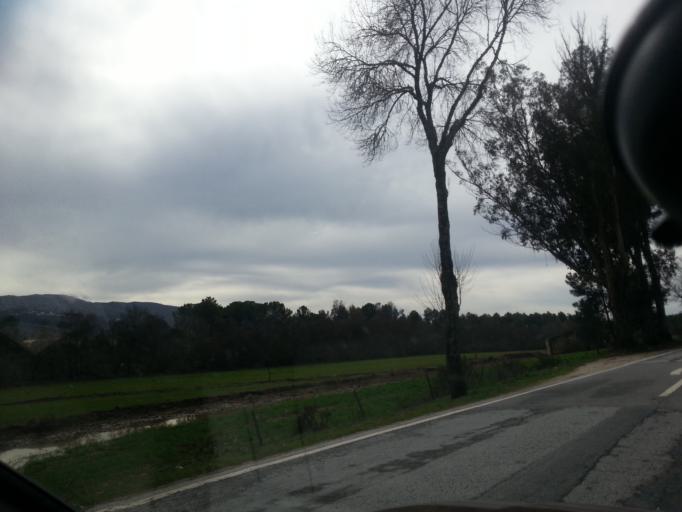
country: PT
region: Guarda
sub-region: Seia
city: Seia
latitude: 40.4551
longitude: -7.6993
